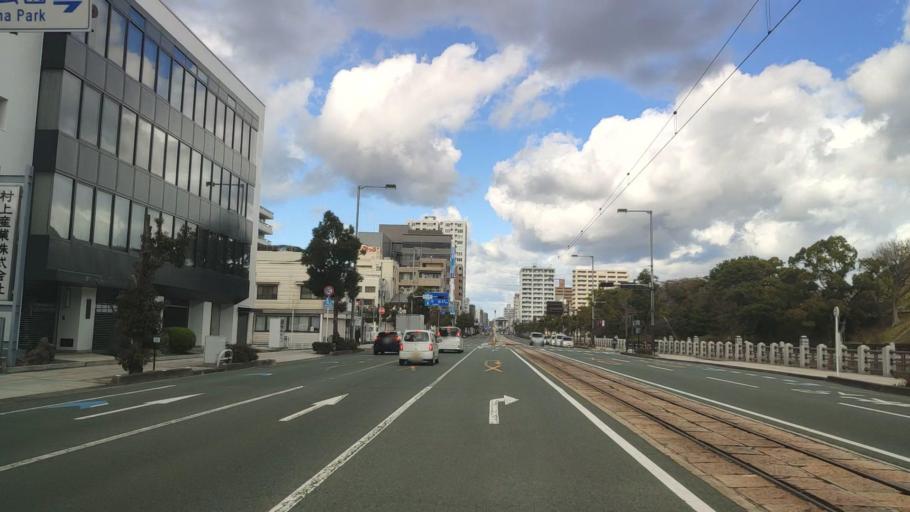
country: JP
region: Ehime
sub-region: Shikoku-chuo Shi
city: Matsuyama
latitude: 33.8410
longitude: 132.7587
